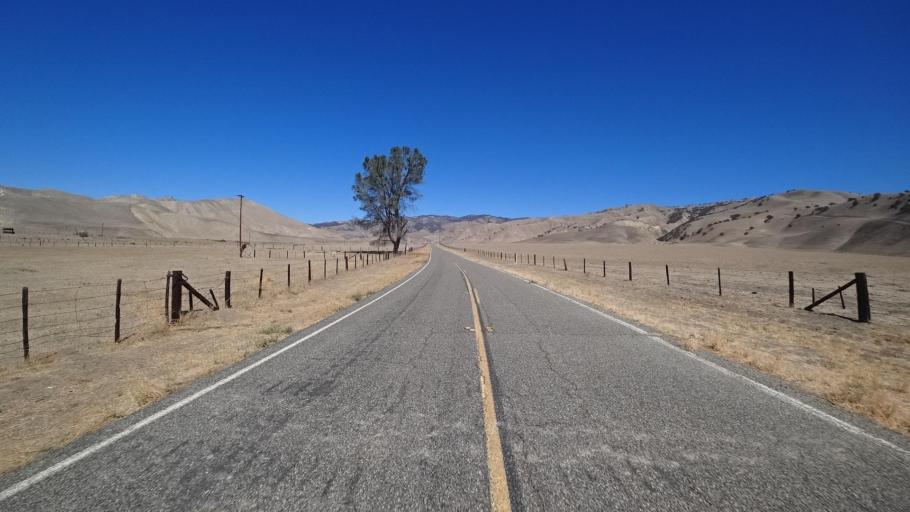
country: US
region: California
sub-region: Monterey County
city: King City
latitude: 36.2805
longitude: -120.9388
